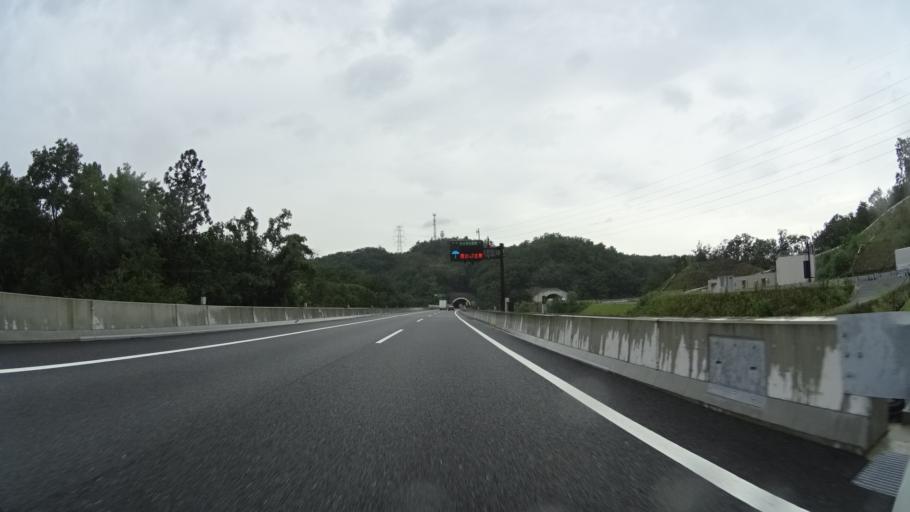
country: JP
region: Osaka
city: Ikeda
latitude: 34.8748
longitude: 135.4223
